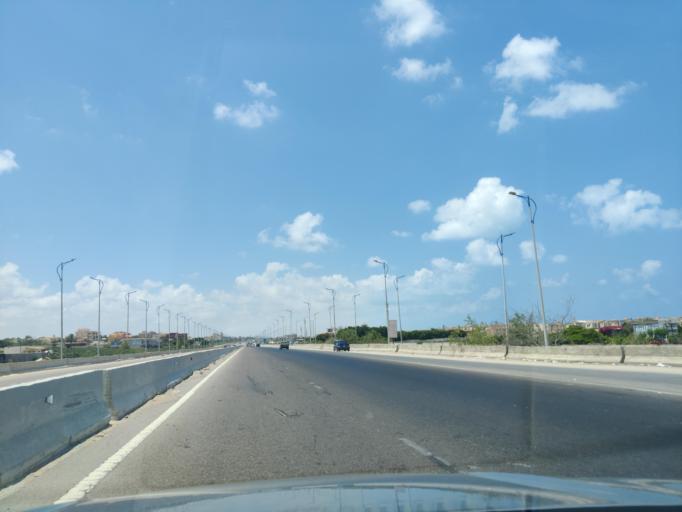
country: EG
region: Alexandria
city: Alexandria
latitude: 30.9802
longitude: 29.5766
